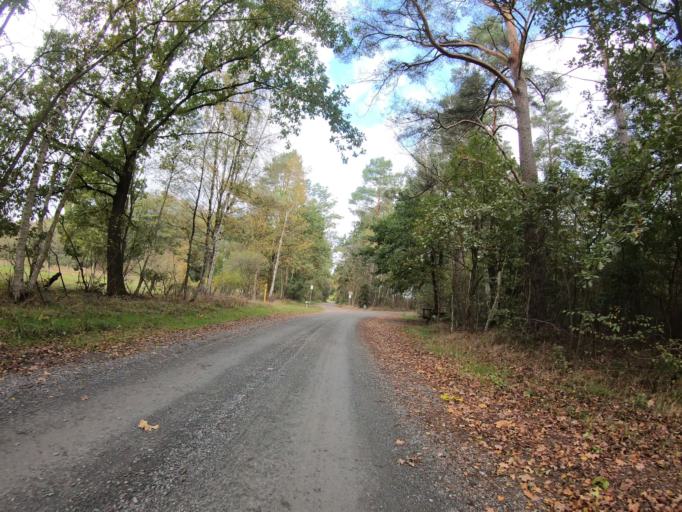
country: DE
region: Lower Saxony
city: Wesendorf
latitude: 52.5679
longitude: 10.5636
